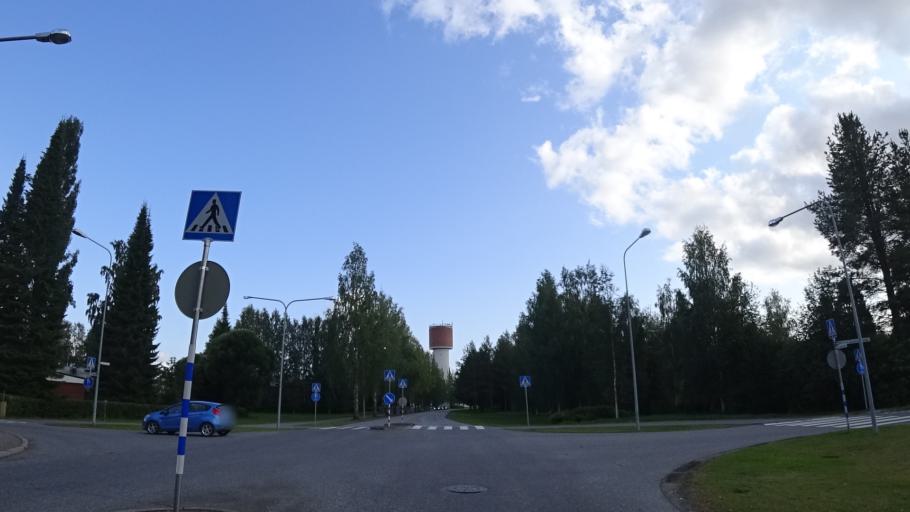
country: FI
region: North Karelia
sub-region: Pielisen Karjala
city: Lieksa
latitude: 63.3243
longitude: 30.0225
